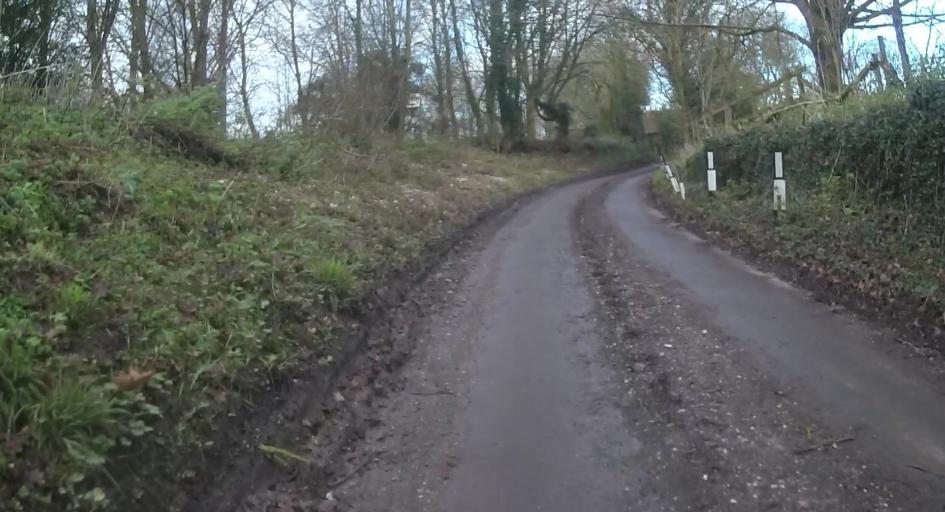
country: GB
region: England
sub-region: Hampshire
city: Tadley
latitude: 51.2874
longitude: -1.1673
